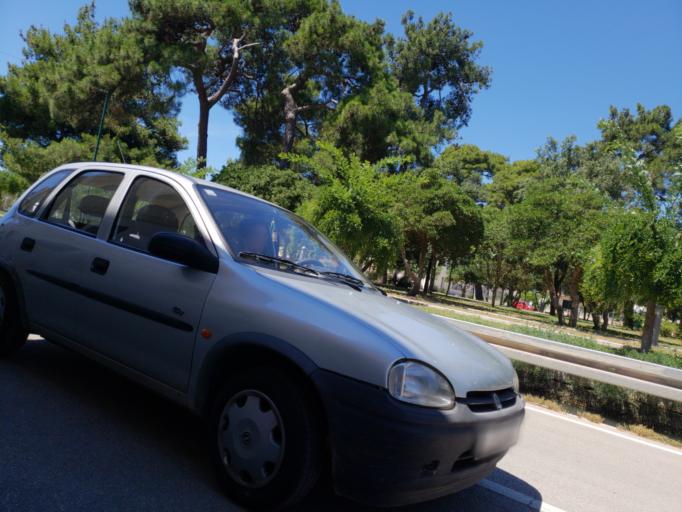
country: HR
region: Splitsko-Dalmatinska
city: Stari Grad
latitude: 43.1841
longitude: 16.6008
